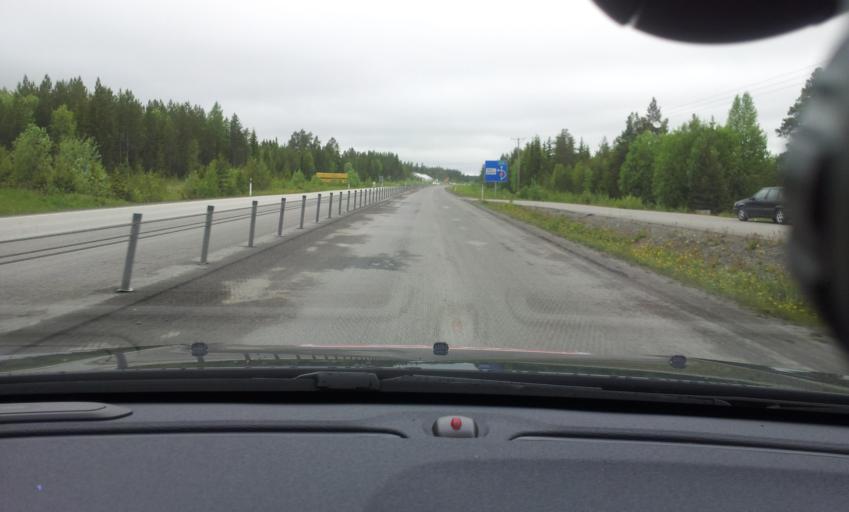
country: SE
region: Jaemtland
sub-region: OEstersunds Kommun
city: Ostersund
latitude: 63.2321
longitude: 14.6117
